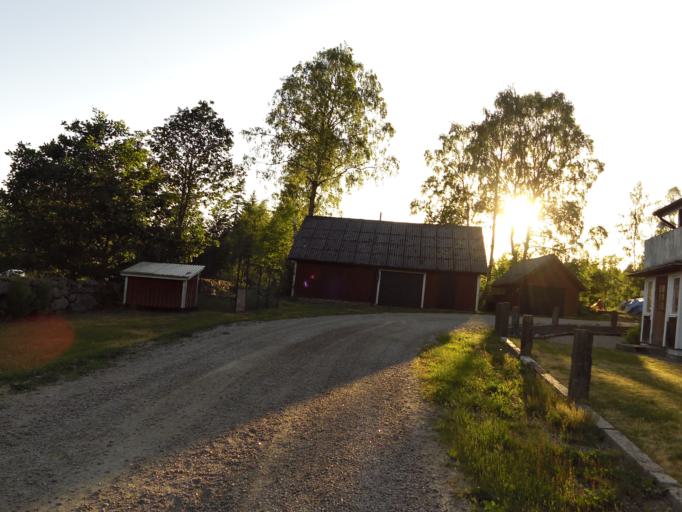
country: SE
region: Blekinge
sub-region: Olofstroms Kommun
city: Olofstroem
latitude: 56.4048
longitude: 14.5663
